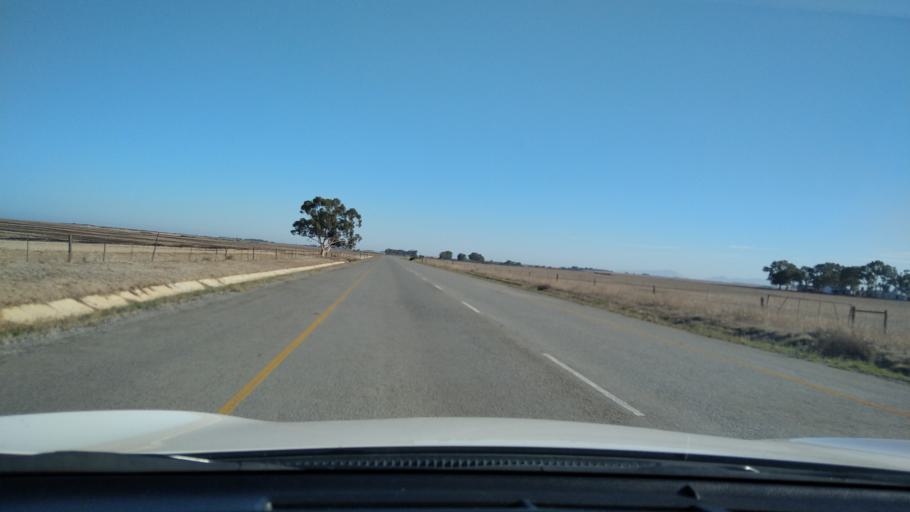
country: ZA
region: Western Cape
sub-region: West Coast District Municipality
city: Moorreesburg
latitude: -33.2861
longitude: 18.6060
